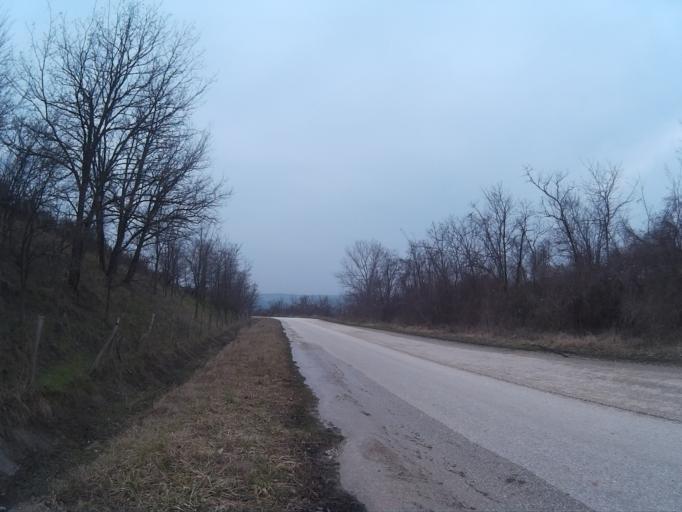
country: HU
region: Fejer
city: Many
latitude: 47.5347
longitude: 18.6021
